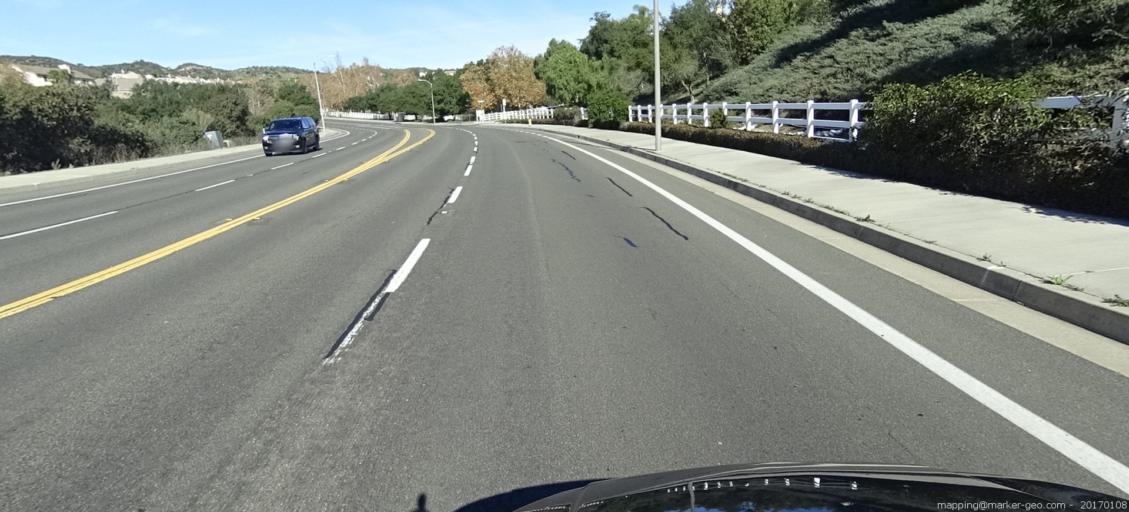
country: US
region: California
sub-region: Orange County
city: Coto De Caza
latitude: 33.5859
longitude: -117.5944
